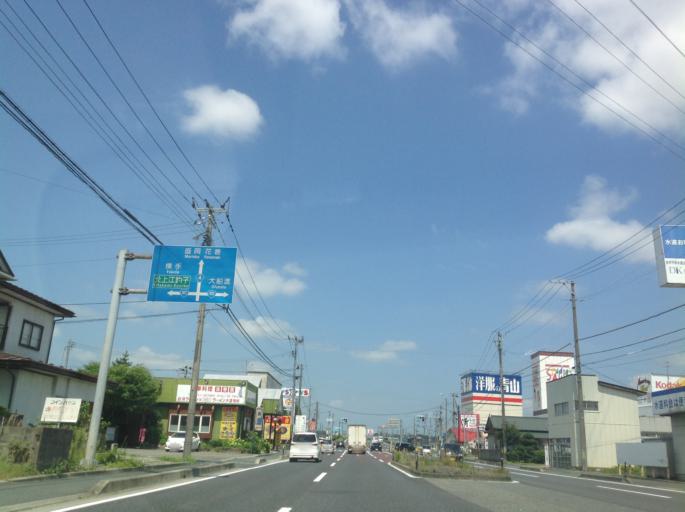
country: JP
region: Iwate
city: Kitakami
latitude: 39.2917
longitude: 141.1050
